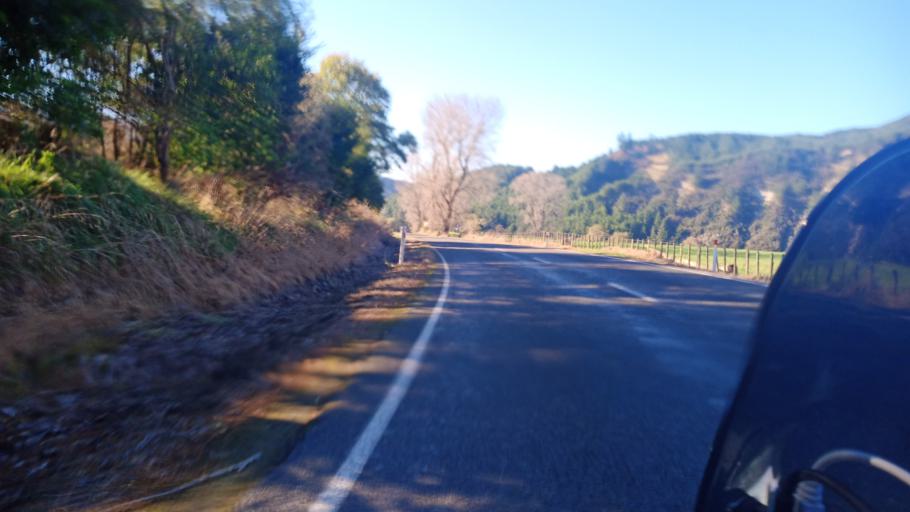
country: NZ
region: Hawke's Bay
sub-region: Wairoa District
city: Wairoa
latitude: -38.8779
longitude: 177.2266
